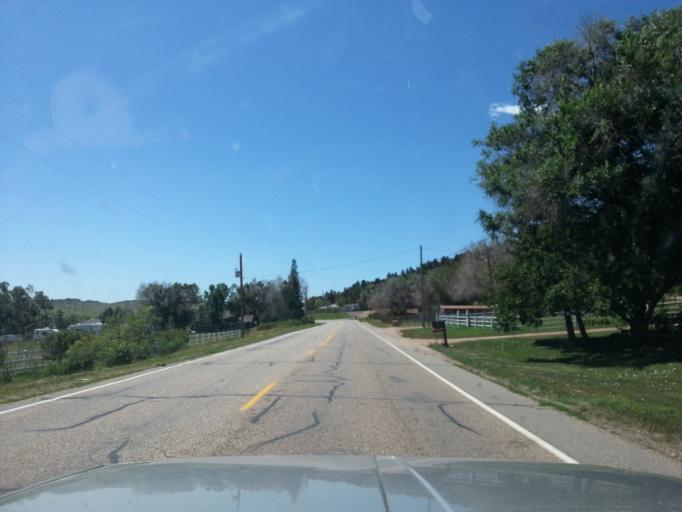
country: US
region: Colorado
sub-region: Larimer County
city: Loveland
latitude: 40.4280
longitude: -105.1930
